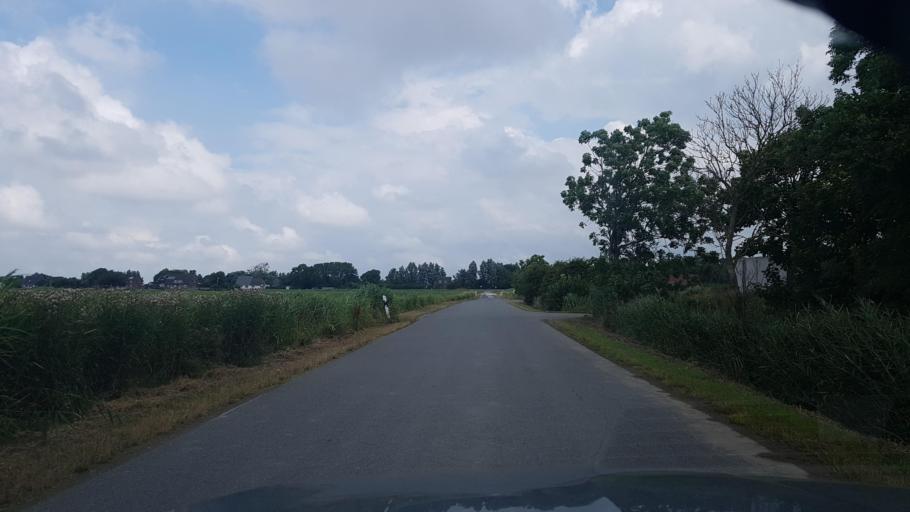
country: DE
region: Schleswig-Holstein
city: Elisabeth-Sophien-Koog
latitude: 54.4991
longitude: 8.8428
